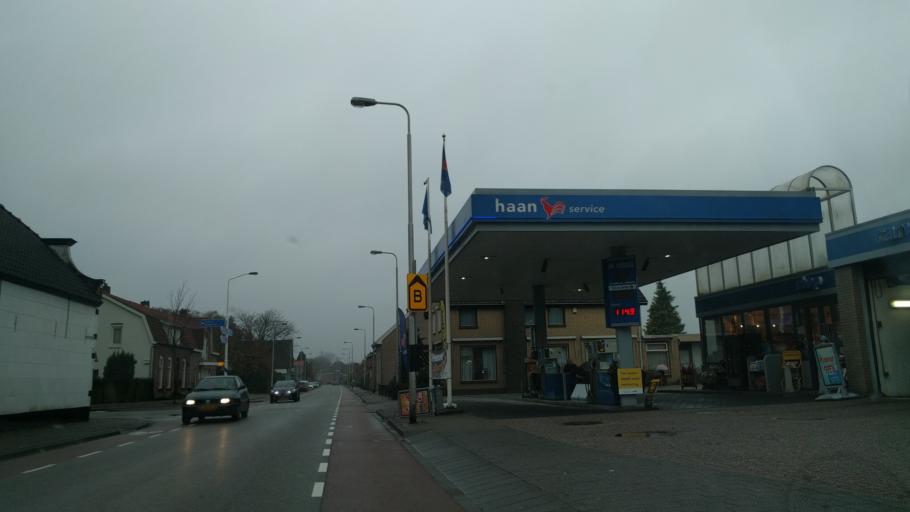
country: NL
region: North Brabant
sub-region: Gemeente Rucphen
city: Rucphen
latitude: 51.5323
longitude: 4.5650
